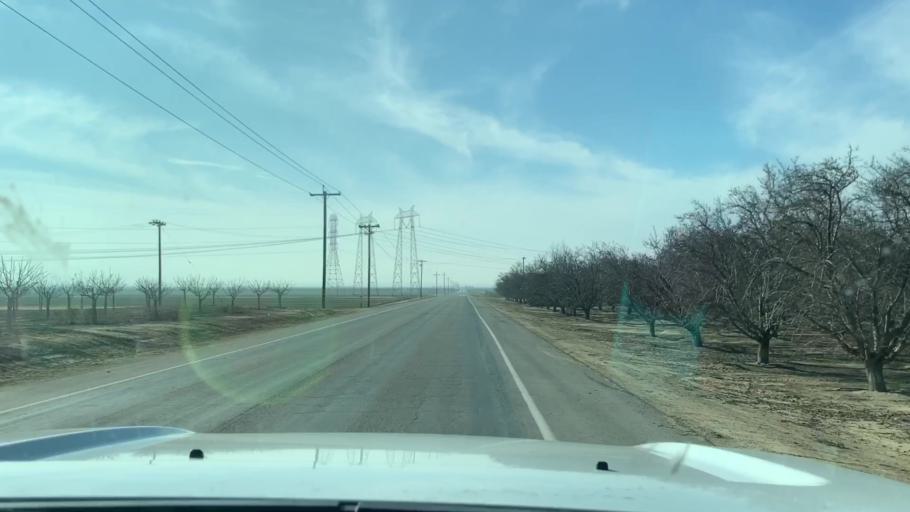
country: US
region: California
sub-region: Kern County
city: Buttonwillow
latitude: 35.4424
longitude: -119.4817
